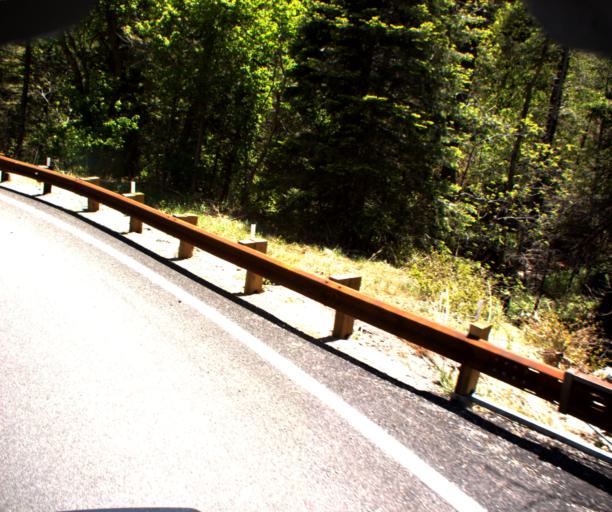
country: US
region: Arizona
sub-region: Coconino County
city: Kachina Village
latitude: 35.0252
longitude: -111.7413
